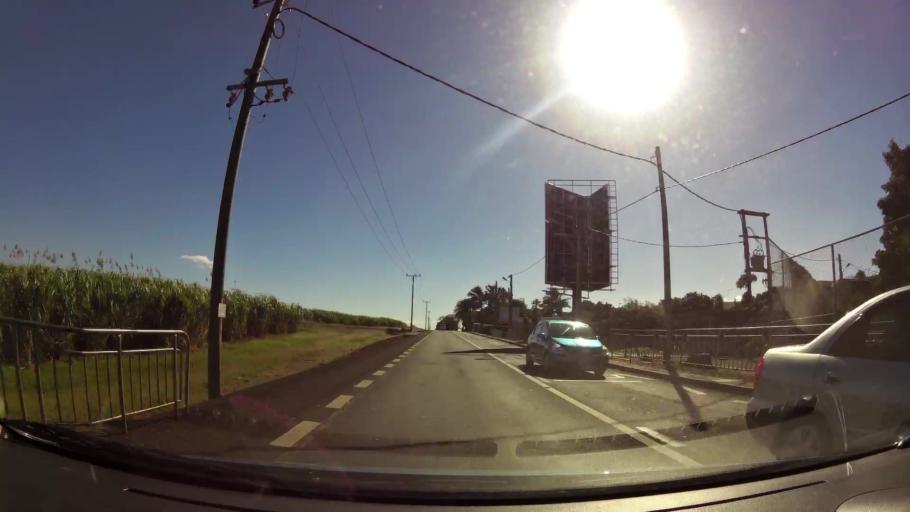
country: MU
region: Black River
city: Cascavelle
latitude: -20.2875
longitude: 57.4029
